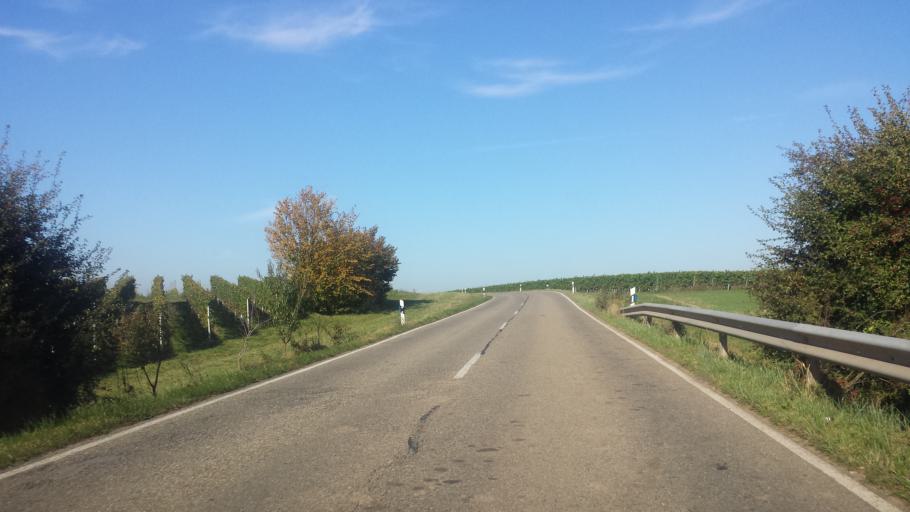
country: DE
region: Rheinland-Pfalz
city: Grossfischlingen
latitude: 49.2546
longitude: 8.1745
